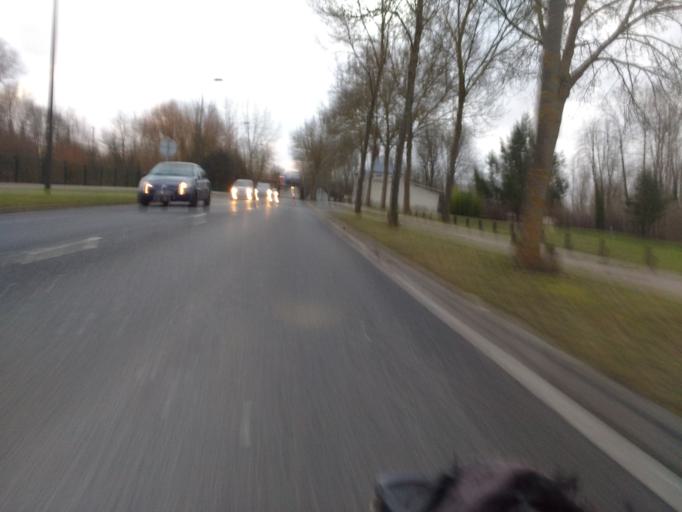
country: FR
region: Picardie
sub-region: Departement de la Somme
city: Camon
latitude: 49.8783
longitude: 2.3384
